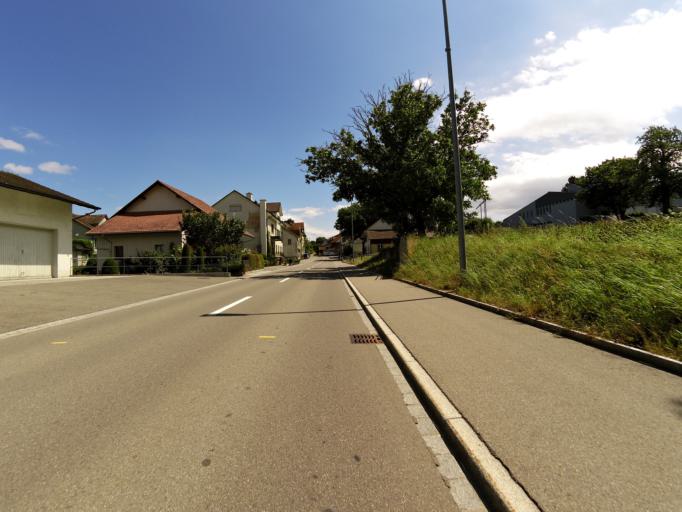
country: CH
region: Thurgau
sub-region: Weinfelden District
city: Wigoltingen
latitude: 47.5974
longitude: 9.0291
